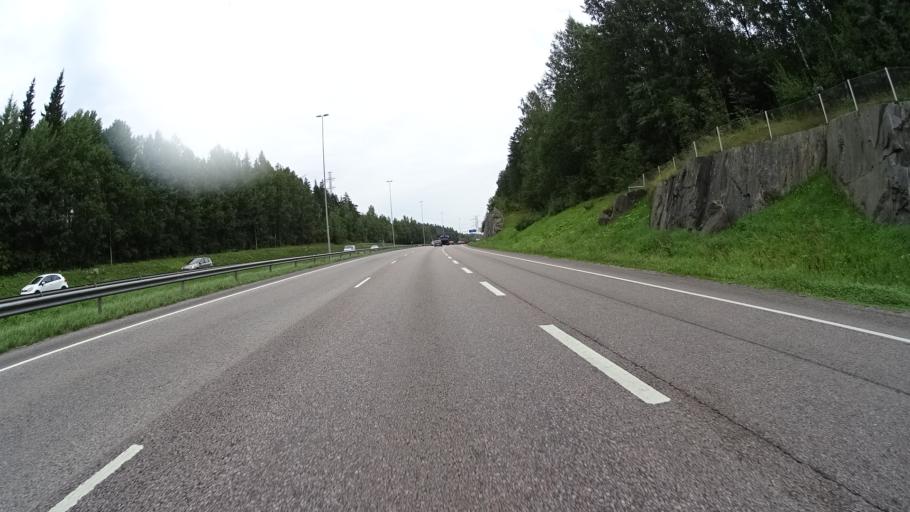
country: FI
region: Uusimaa
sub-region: Helsinki
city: Teekkarikylae
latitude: 60.2964
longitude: 24.8685
